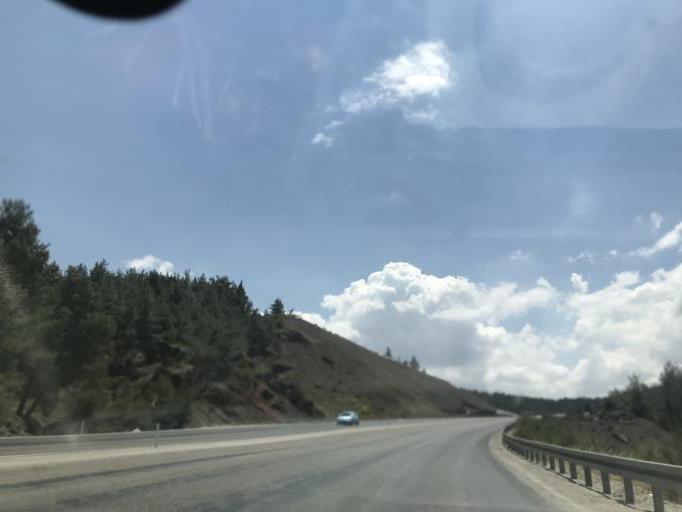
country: TR
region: Denizli
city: Serinhisar
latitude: 37.6561
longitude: 29.2282
